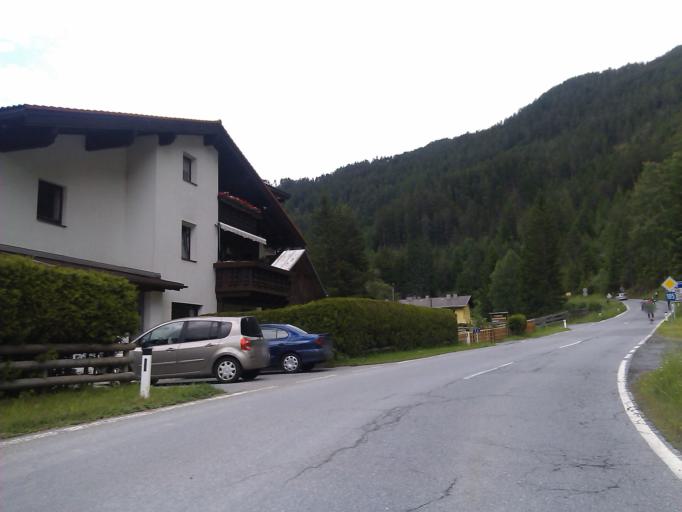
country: AT
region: Tyrol
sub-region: Politischer Bezirk Landeck
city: Nauders
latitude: 46.8857
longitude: 10.4670
